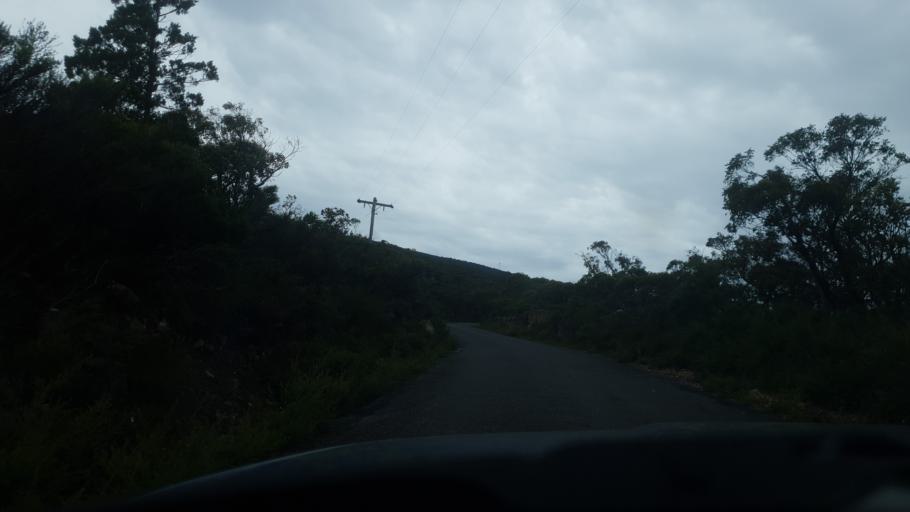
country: AU
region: Victoria
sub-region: Northern Grampians
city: Stawell
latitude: -37.2804
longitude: 142.5858
